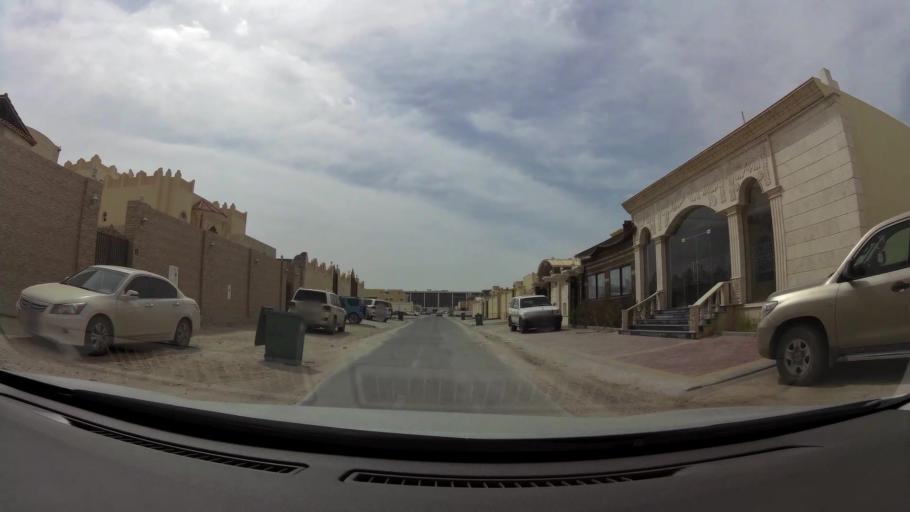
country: QA
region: Al Wakrah
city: Al Wukayr
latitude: 25.1989
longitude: 51.4590
